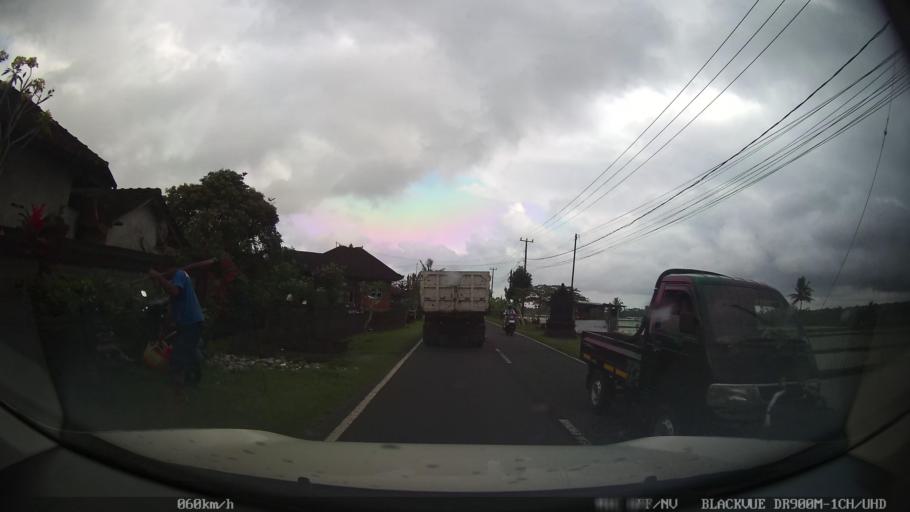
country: ID
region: Bali
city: Empalan
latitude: -8.4030
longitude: 115.1474
